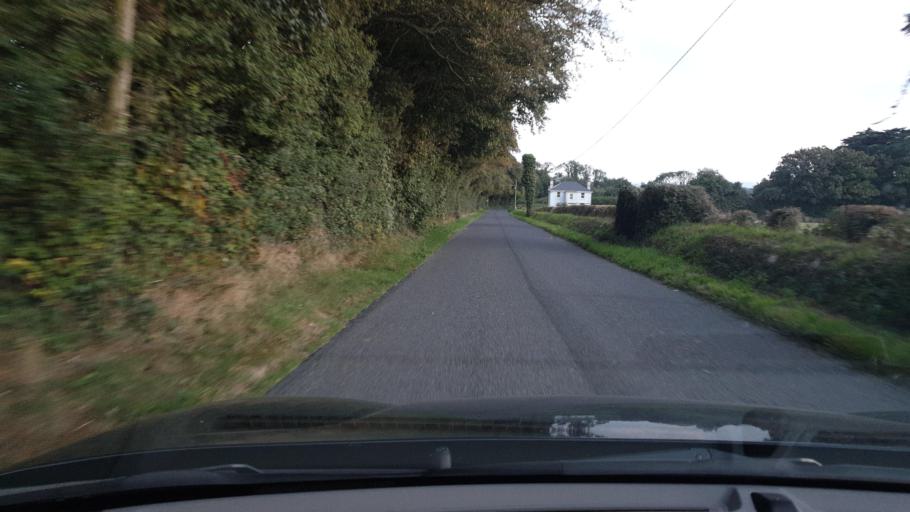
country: IE
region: Leinster
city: Balrothery
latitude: 53.5721
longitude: -6.1555
